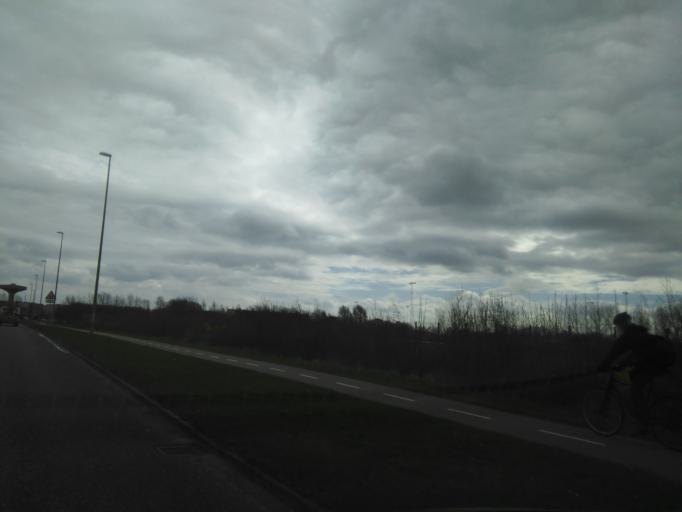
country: DK
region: Central Jutland
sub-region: Arhus Kommune
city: Stavtrup
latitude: 56.1717
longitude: 10.1450
